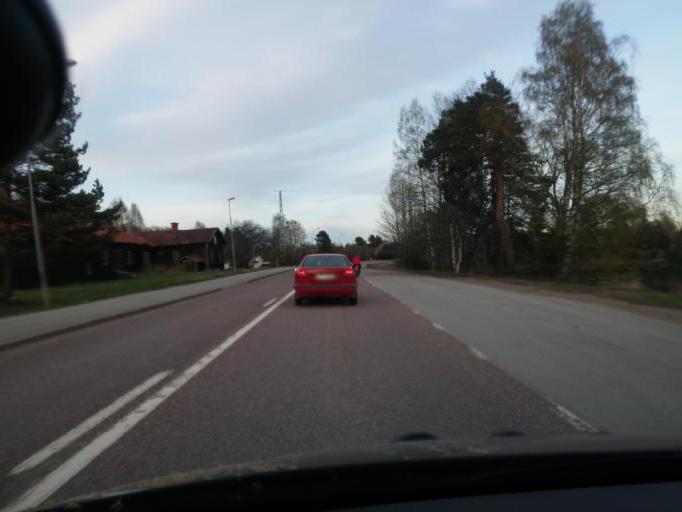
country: SE
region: Gaevleborg
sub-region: Ljusdals Kommun
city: Ljusdal
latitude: 61.8375
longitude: 16.0584
